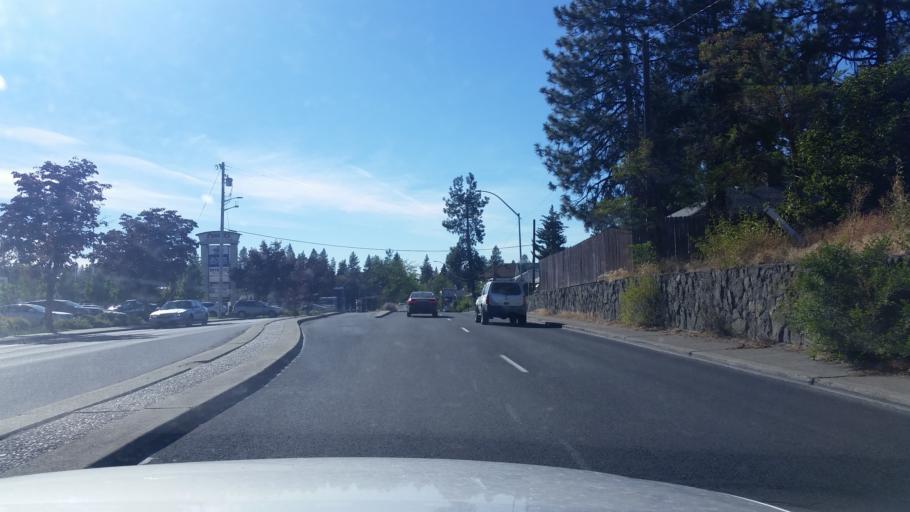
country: US
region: Washington
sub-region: Spokane County
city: Spokane
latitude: 47.6282
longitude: -117.3983
